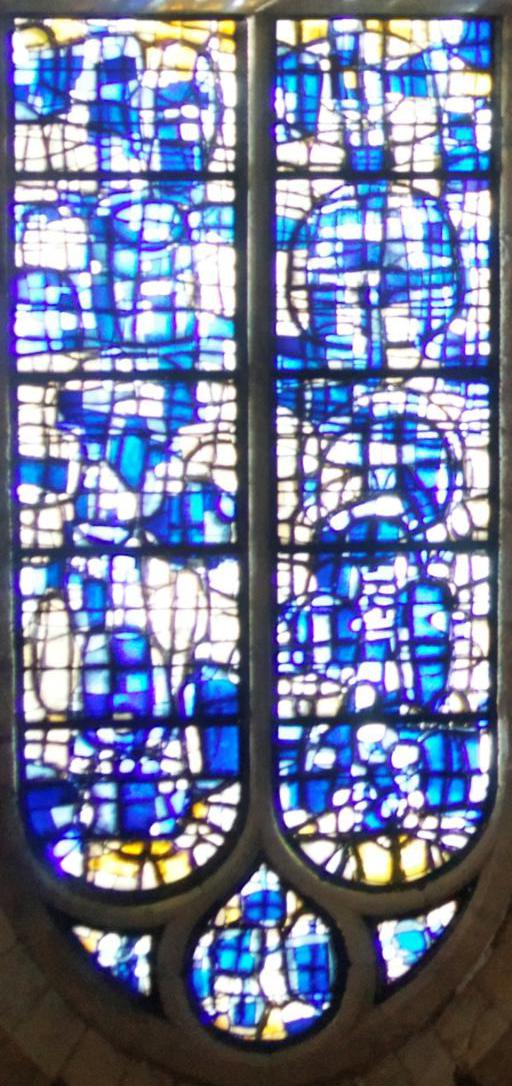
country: FR
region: Haute-Normandie
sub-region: Departement de la Seine-Maritime
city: Varengeville-sur-Mer
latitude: 49.9168
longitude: 0.9825
